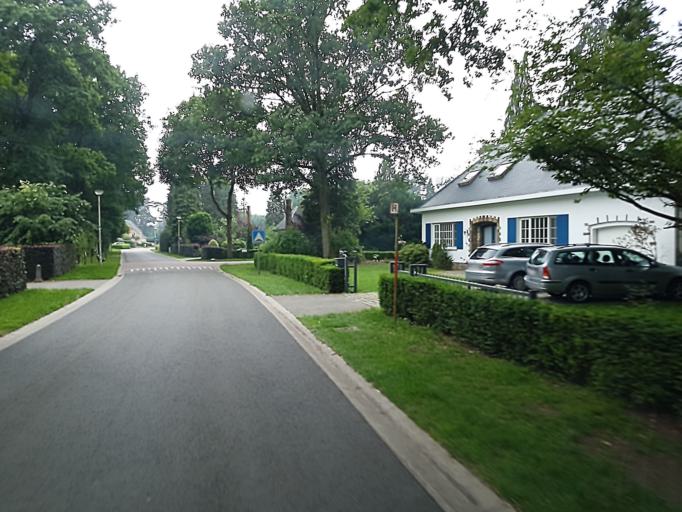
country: BE
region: Flanders
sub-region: Provincie Antwerpen
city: Zoersel
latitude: 51.2673
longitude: 4.7049
